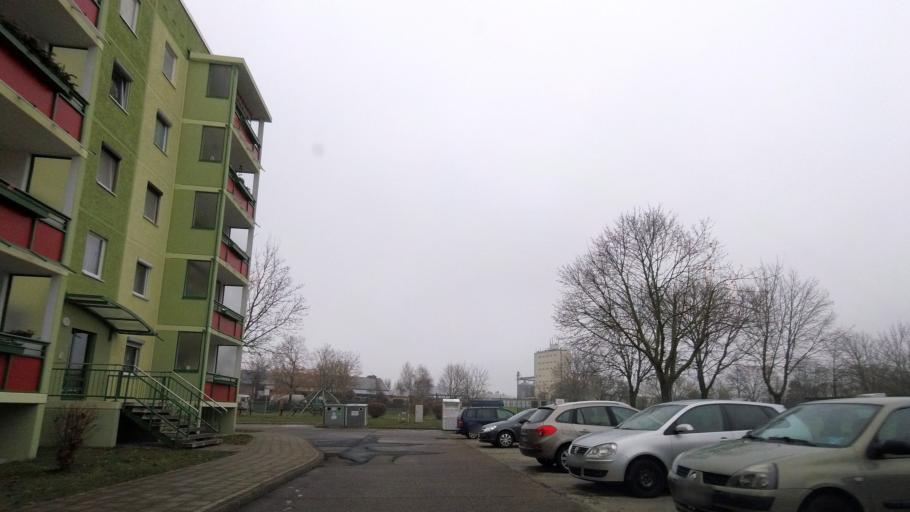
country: DE
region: Brandenburg
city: Juterbog
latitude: 52.0036
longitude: 13.0737
